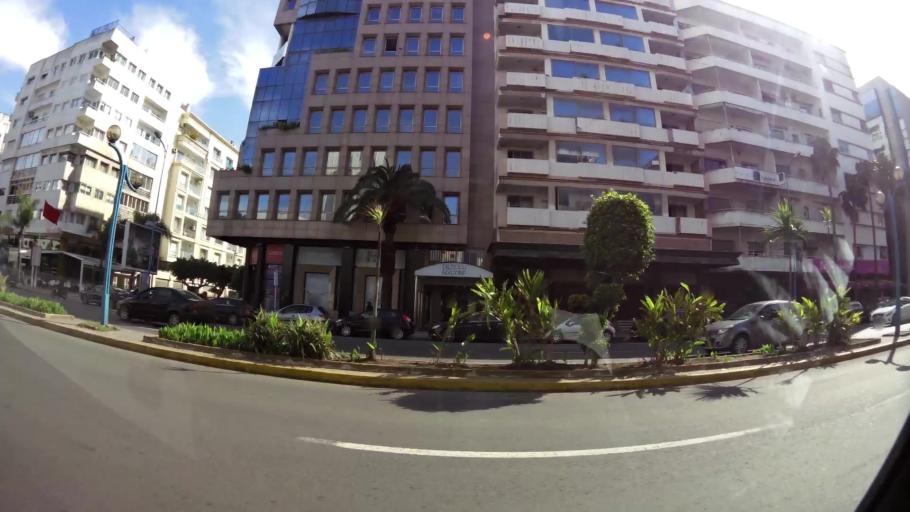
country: MA
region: Grand Casablanca
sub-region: Casablanca
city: Casablanca
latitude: 33.5891
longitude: -7.6332
